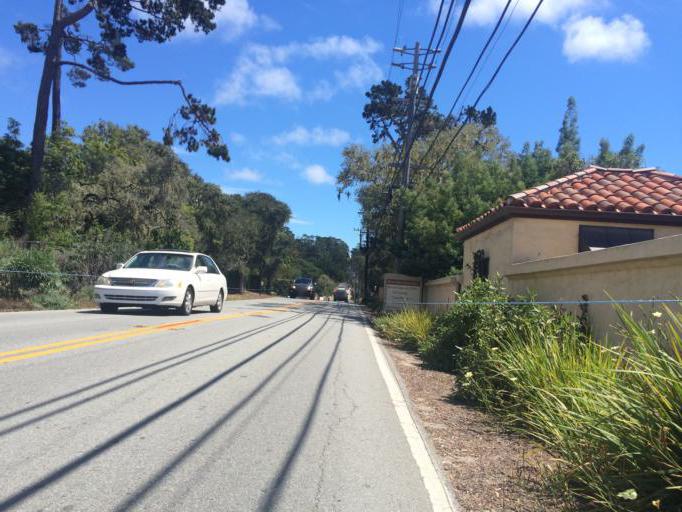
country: US
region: California
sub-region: Monterey County
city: Del Monte Forest
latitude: 36.5706
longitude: -121.9410
